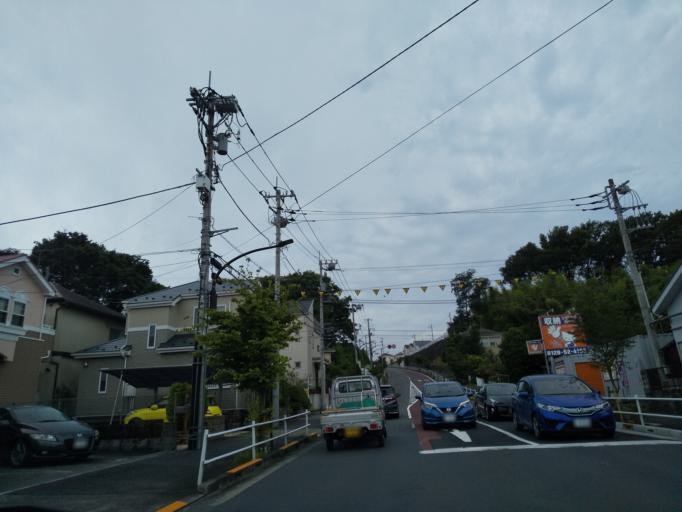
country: JP
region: Tokyo
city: Hino
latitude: 35.6849
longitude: 139.3808
